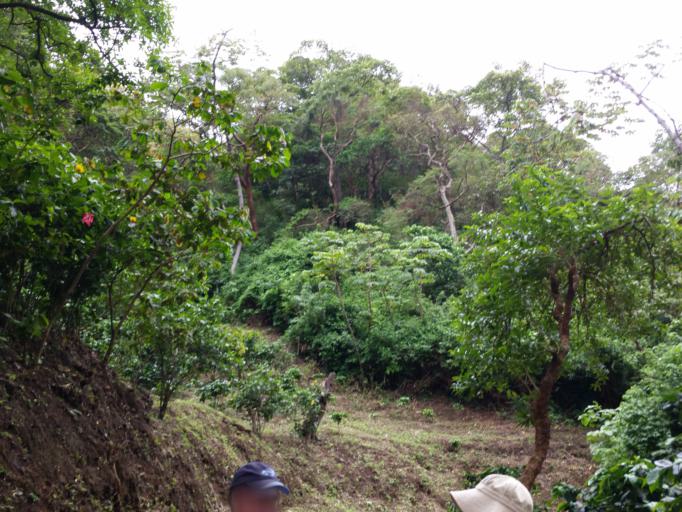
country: NI
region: Managua
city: El Crucero
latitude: 11.9857
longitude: -86.2863
